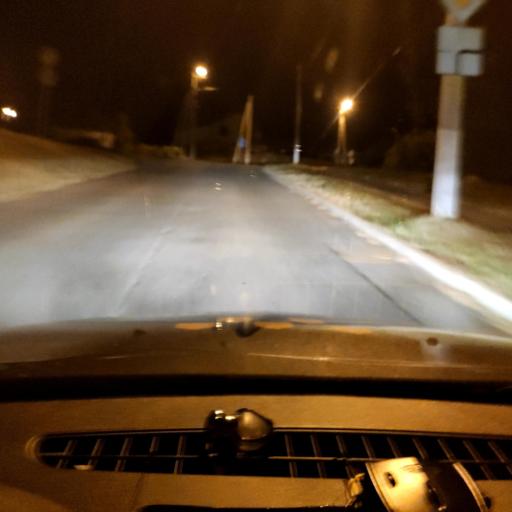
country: RU
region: Belgorod
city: Mayskiy
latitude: 50.5141
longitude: 36.4665
